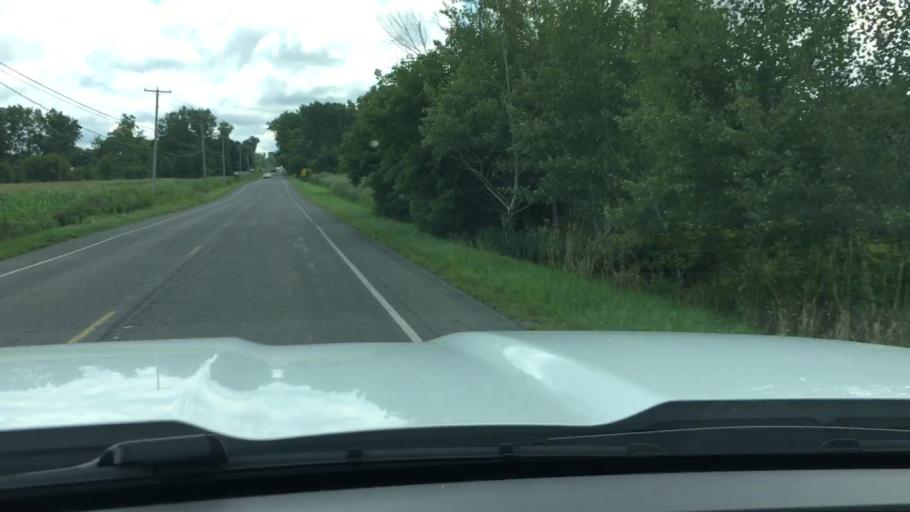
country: US
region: Michigan
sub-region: Eaton County
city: Dimondale
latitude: 42.5821
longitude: -84.5902
